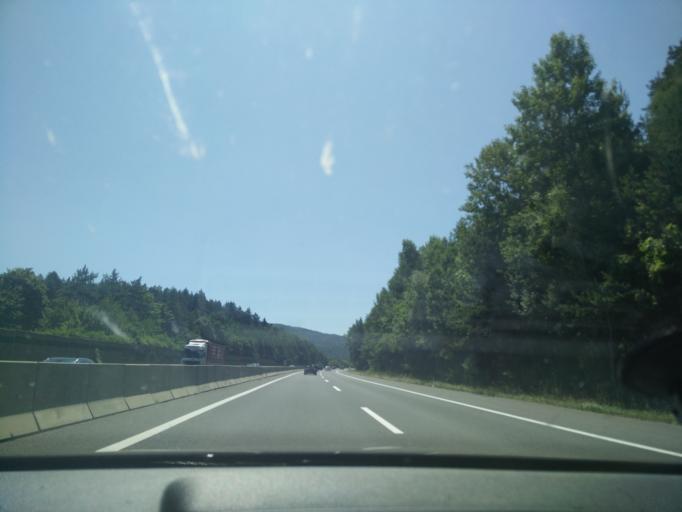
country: AT
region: Lower Austria
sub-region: Politischer Bezirk Neunkirchen
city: Seebenstein
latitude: 47.6744
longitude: 16.1252
